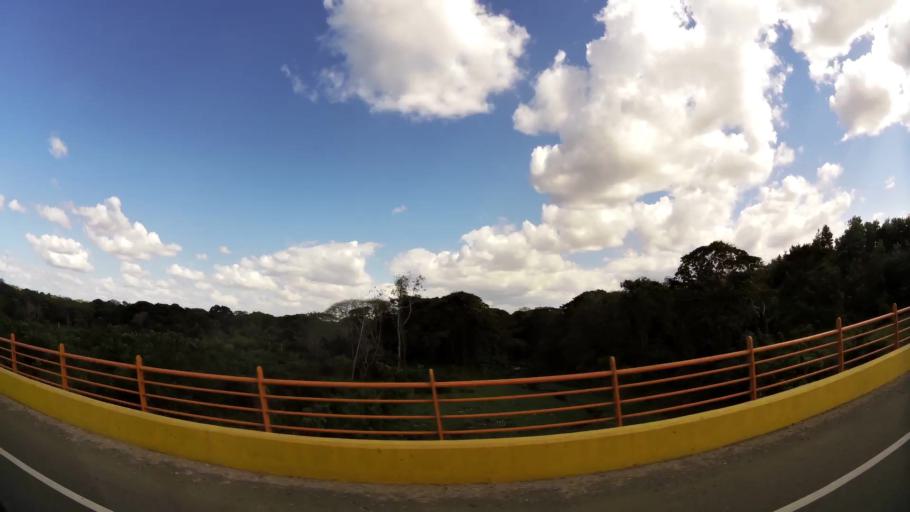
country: DO
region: Santo Domingo
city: Santo Domingo Oeste
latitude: 18.5536
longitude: -70.0730
